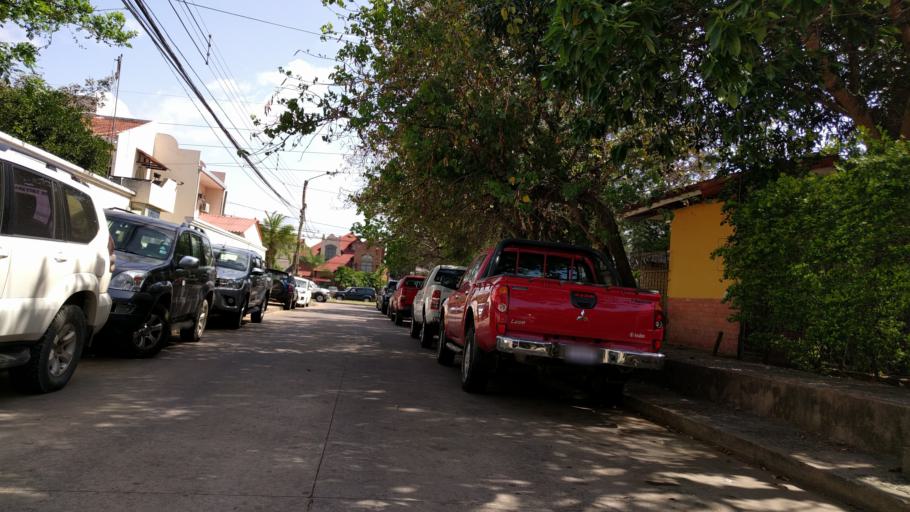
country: BO
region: Santa Cruz
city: Santa Cruz de la Sierra
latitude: -17.7866
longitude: -63.2129
